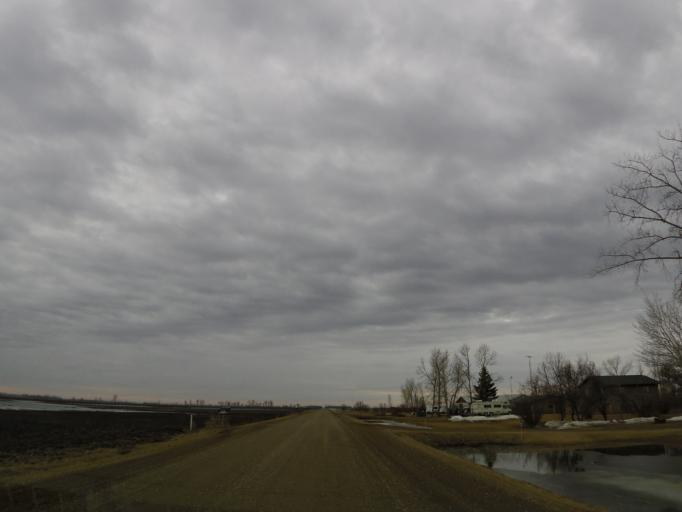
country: US
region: North Dakota
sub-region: Walsh County
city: Grafton
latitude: 48.4103
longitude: -97.4485
